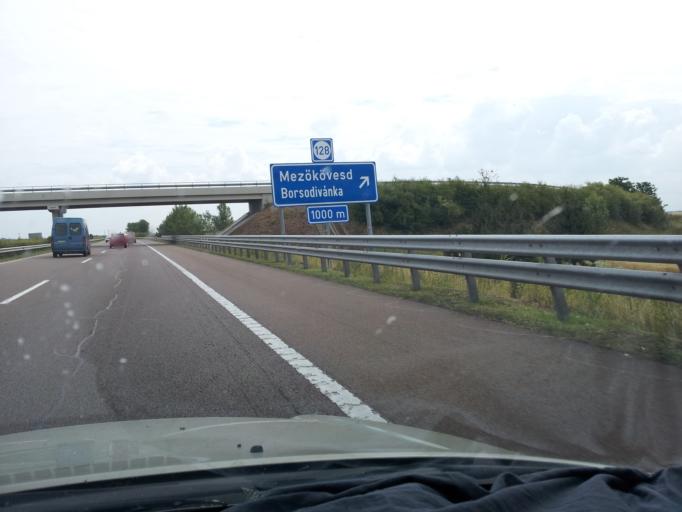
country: HU
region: Borsod-Abauj-Zemplen
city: Mezokovesd
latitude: 47.7730
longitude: 20.5629
